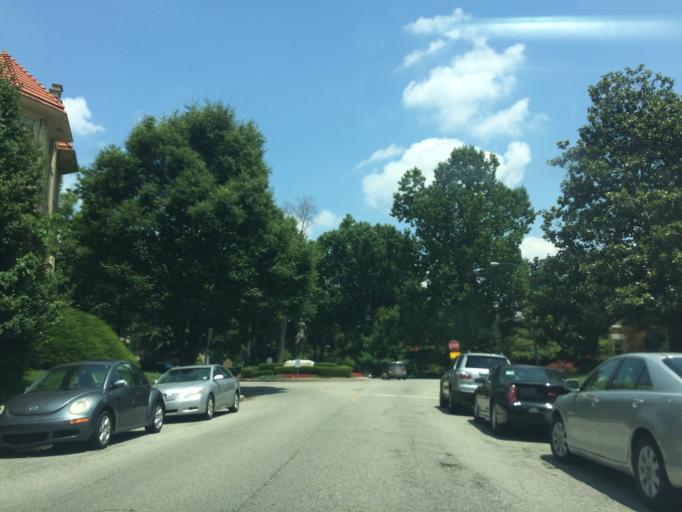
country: US
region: Kentucky
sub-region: Jefferson County
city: Audubon Park
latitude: 38.2350
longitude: -85.7130
